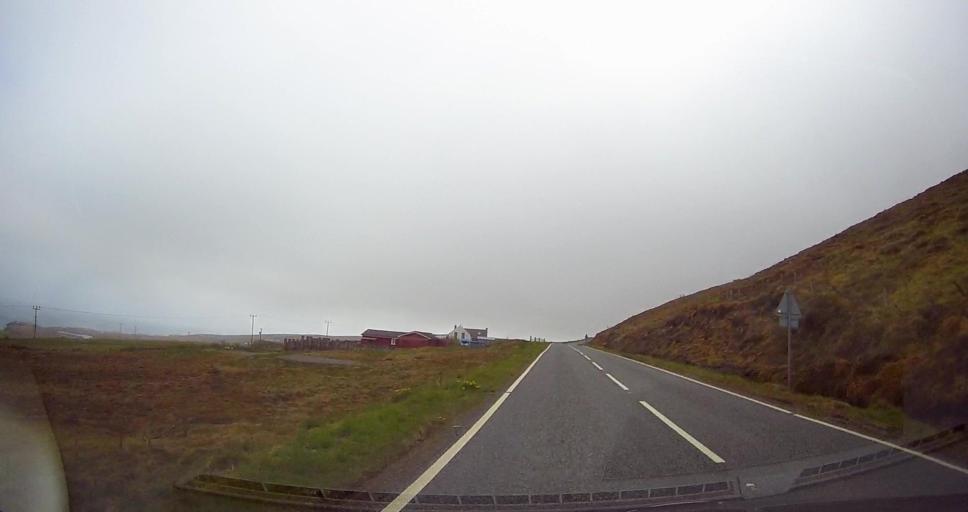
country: GB
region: Scotland
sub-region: Shetland Islands
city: Sandwick
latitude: 59.9740
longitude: -1.2770
